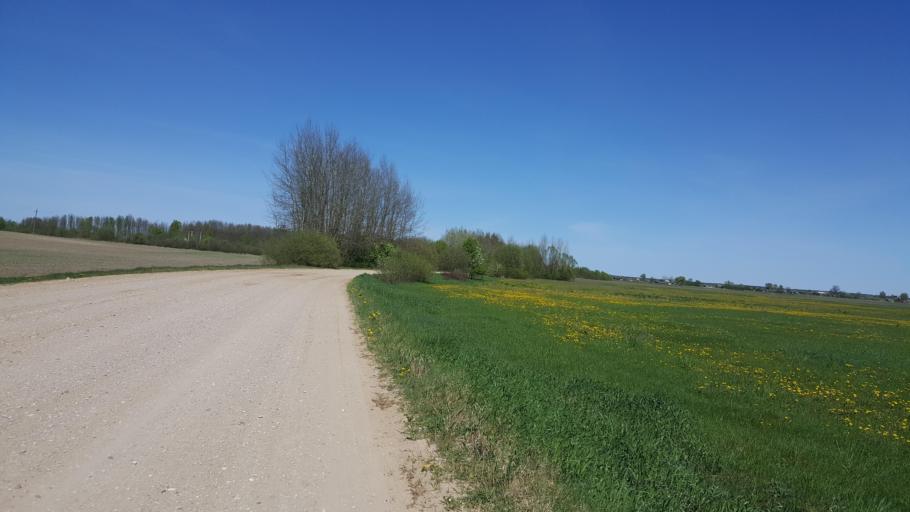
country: BY
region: Brest
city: Kamyanyets
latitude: 52.4484
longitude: 23.8657
